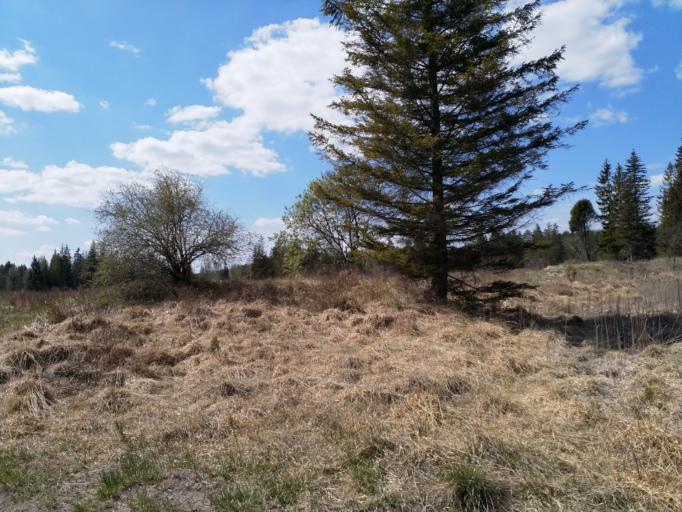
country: LV
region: Kandava
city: Kandava
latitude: 57.0177
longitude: 22.7789
